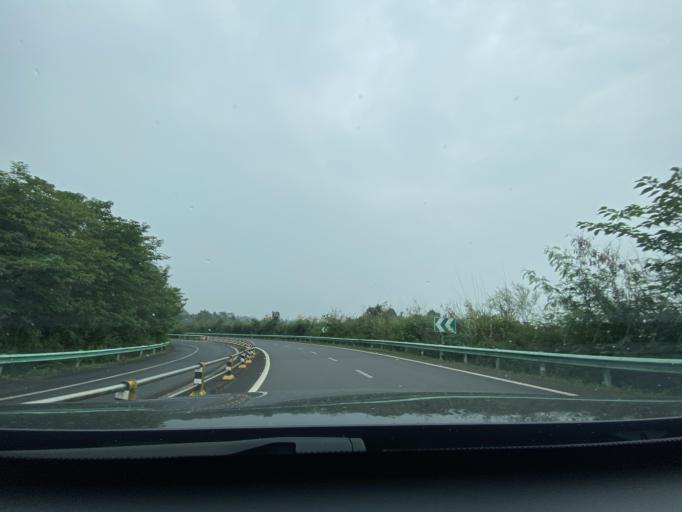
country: CN
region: Sichuan
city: Wenlin
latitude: 30.2967
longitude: 104.1249
